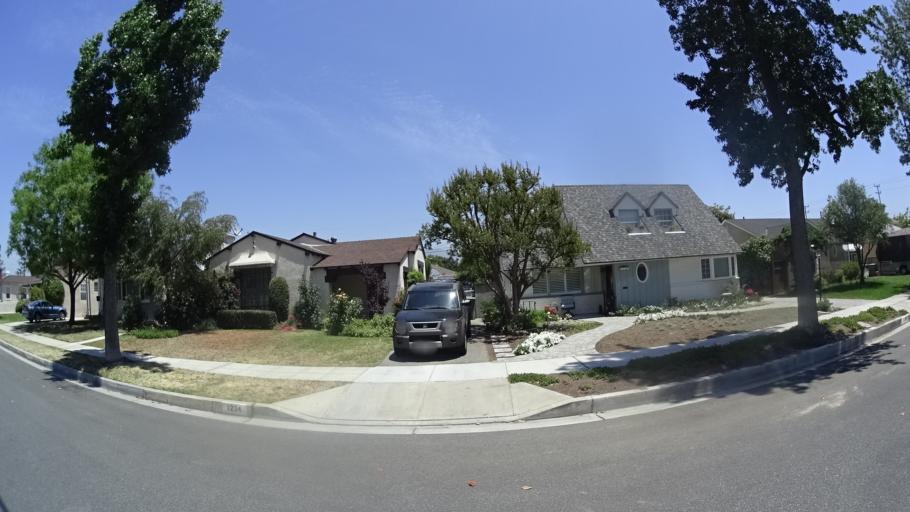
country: US
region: California
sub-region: Los Angeles County
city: North Hollywood
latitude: 34.1736
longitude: -118.3463
